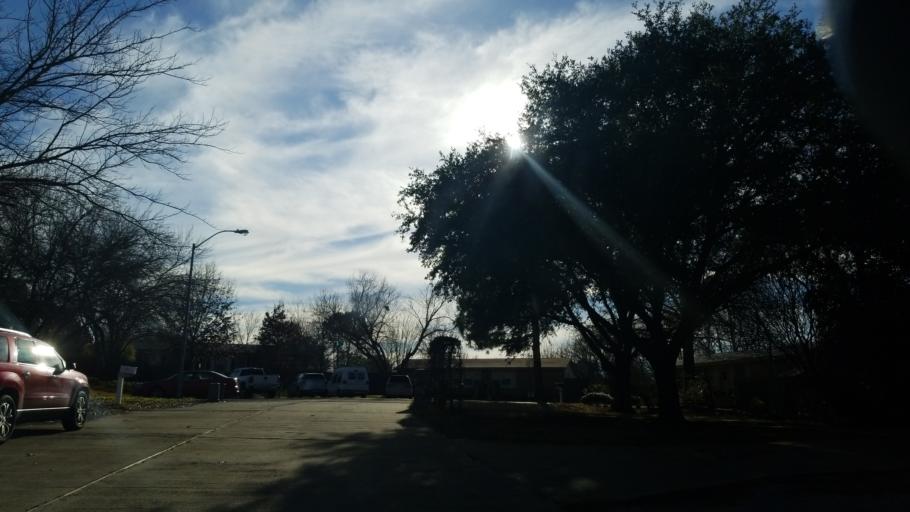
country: US
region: Texas
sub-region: Denton County
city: Corinth
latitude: 33.1387
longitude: -97.0626
